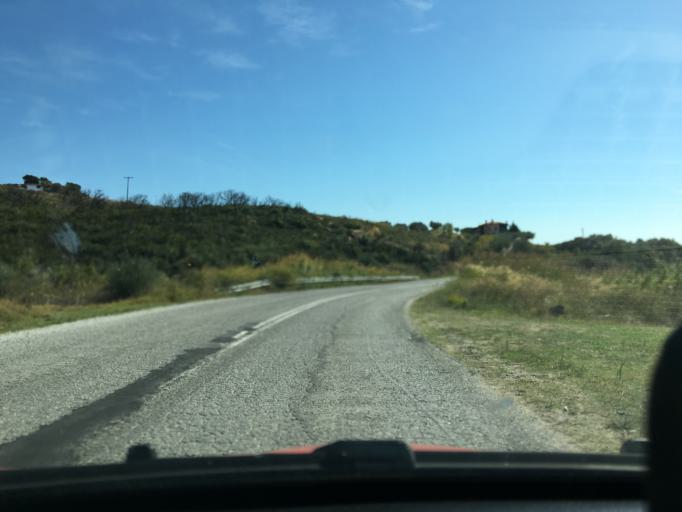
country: GR
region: Central Macedonia
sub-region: Nomos Chalkidikis
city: Ouranoupolis
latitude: 40.3520
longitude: 23.9549
